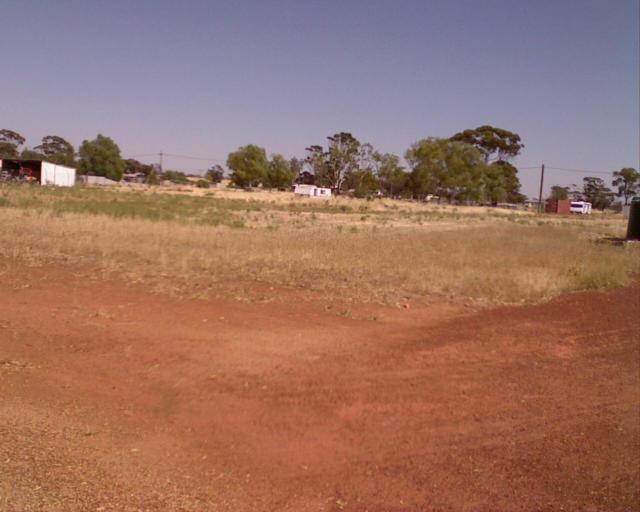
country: AU
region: Western Australia
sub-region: Merredin
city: Merredin
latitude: -31.6087
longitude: 117.8788
